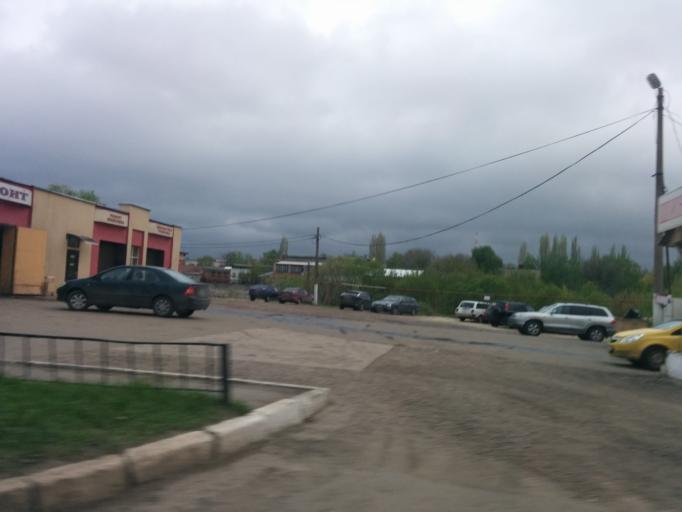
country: RU
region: Tambov
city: Tambov
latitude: 52.7311
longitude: 41.4342
